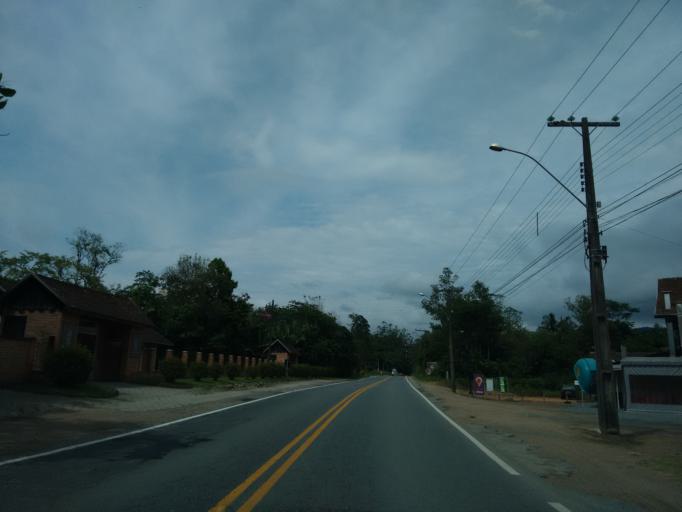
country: BR
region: Santa Catarina
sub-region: Pomerode
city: Pomerode
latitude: -26.6876
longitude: -49.1512
